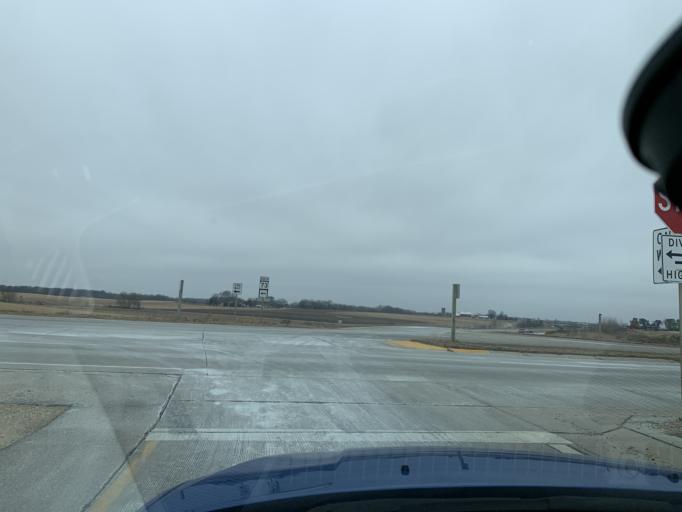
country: US
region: Wisconsin
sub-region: Columbia County
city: Columbus
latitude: 43.3181
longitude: -89.0439
